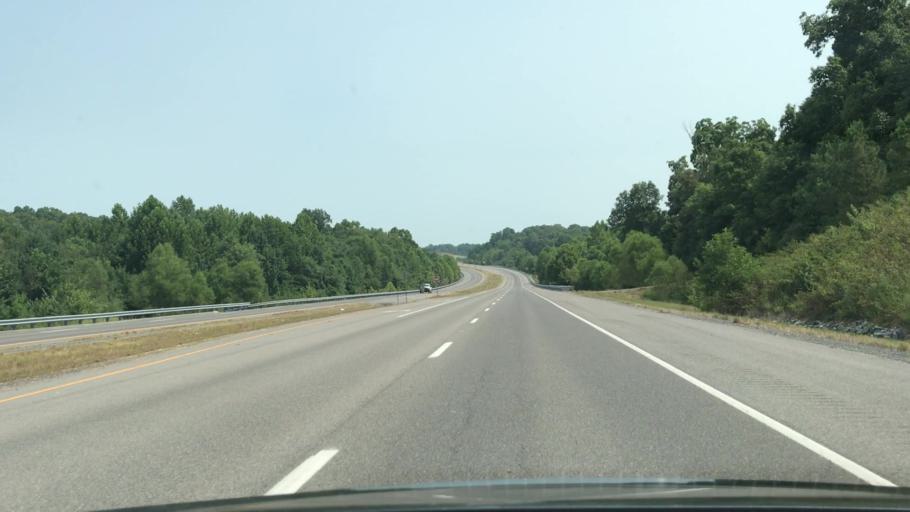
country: US
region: Kentucky
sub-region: Calloway County
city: Murray
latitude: 36.7538
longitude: -88.1544
